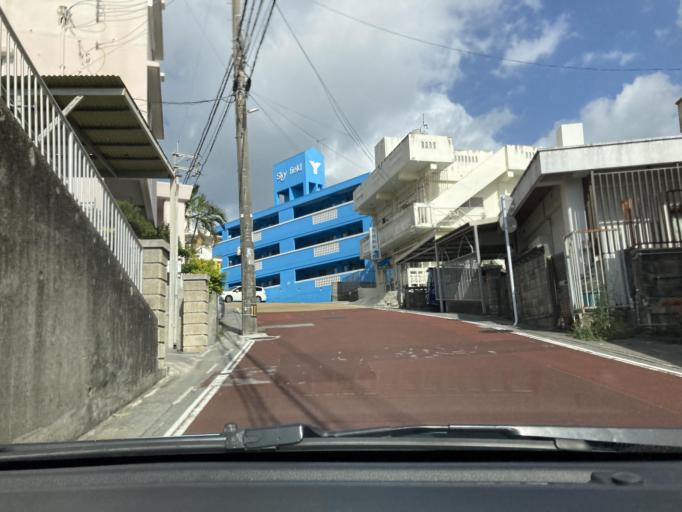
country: JP
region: Okinawa
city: Naha-shi
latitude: 26.1999
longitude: 127.7045
